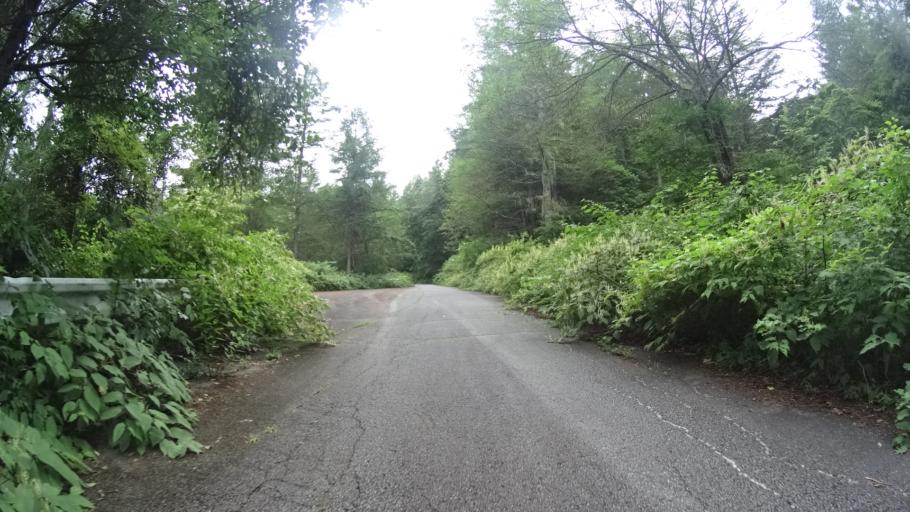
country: JP
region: Yamanashi
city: Enzan
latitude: 35.8055
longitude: 138.6332
